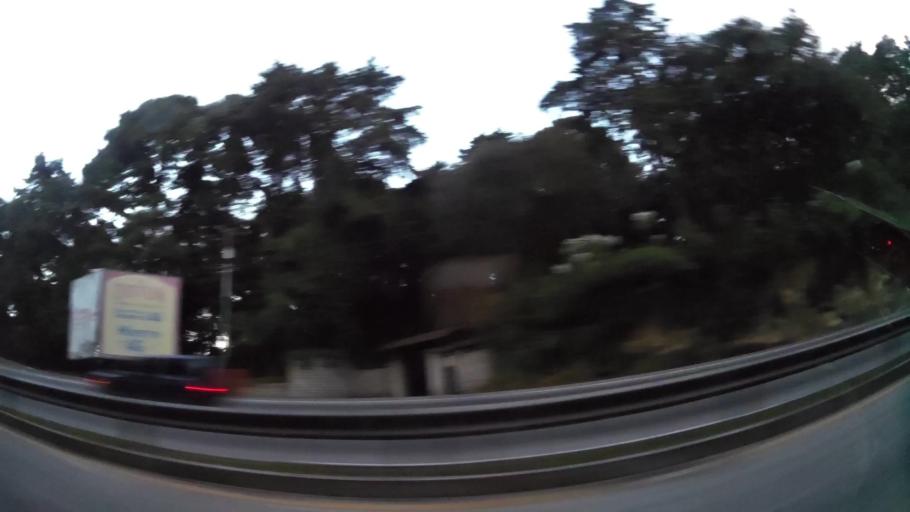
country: GT
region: Sacatepequez
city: San Lucas Sacatepequez
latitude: 14.6070
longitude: -90.6262
